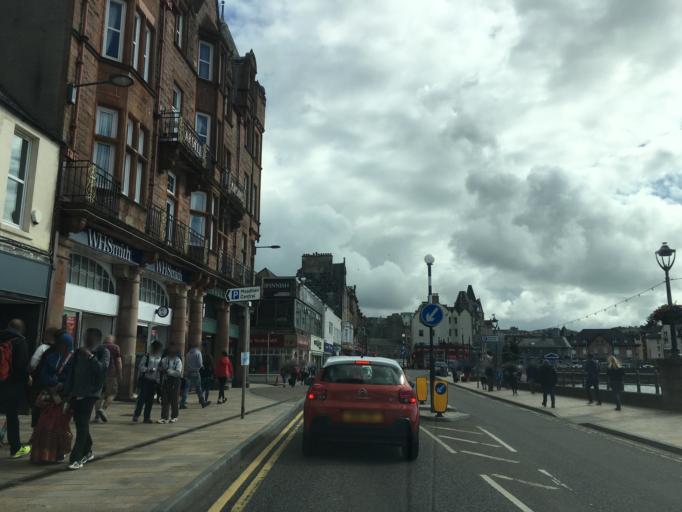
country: GB
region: Scotland
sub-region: Argyll and Bute
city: Oban
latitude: 56.4145
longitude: -5.4726
